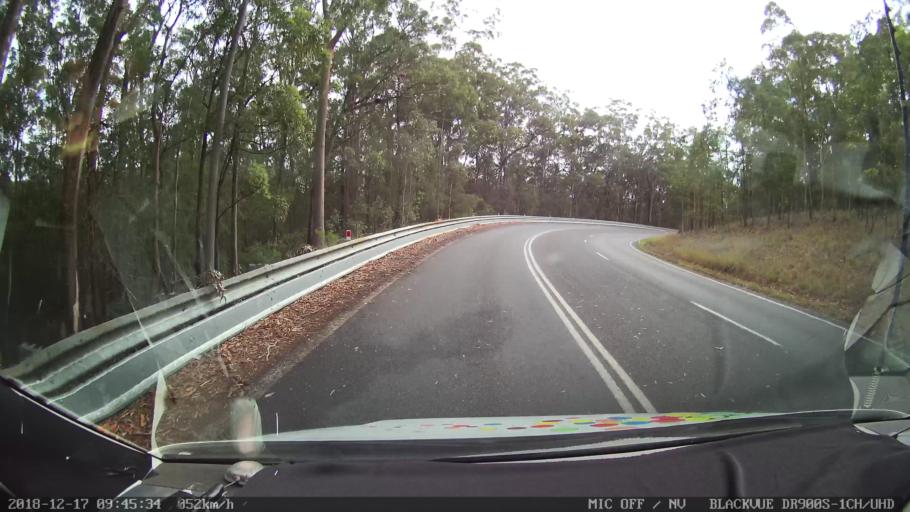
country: AU
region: New South Wales
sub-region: Tenterfield Municipality
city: Carrolls Creek
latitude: -28.9251
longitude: 152.3306
